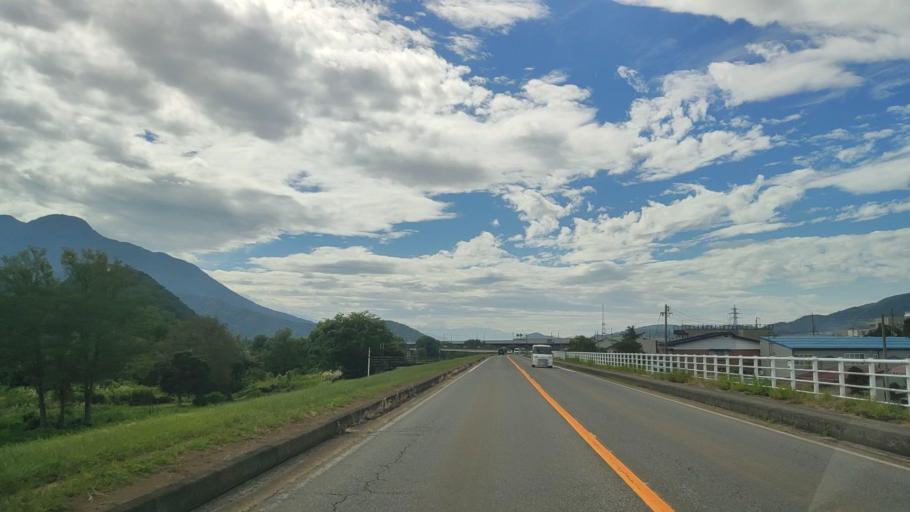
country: JP
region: Nagano
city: Iiyama
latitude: 36.8466
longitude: 138.3648
